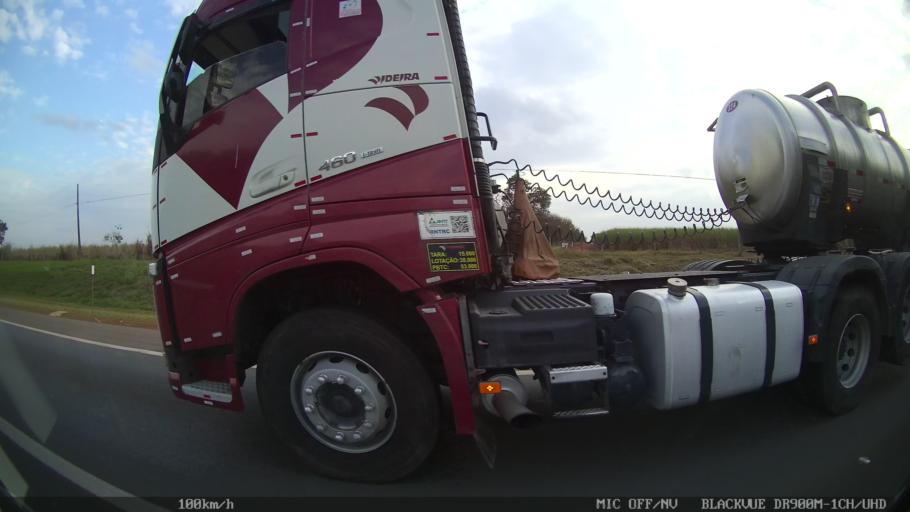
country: BR
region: Sao Paulo
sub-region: Americana
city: Americana
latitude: -22.6682
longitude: -47.3153
